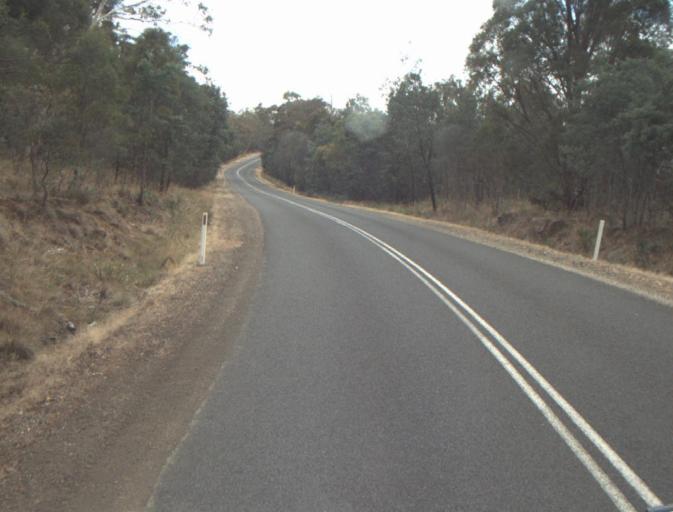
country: AU
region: Tasmania
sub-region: Northern Midlands
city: Evandale
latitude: -41.4971
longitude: 147.3847
